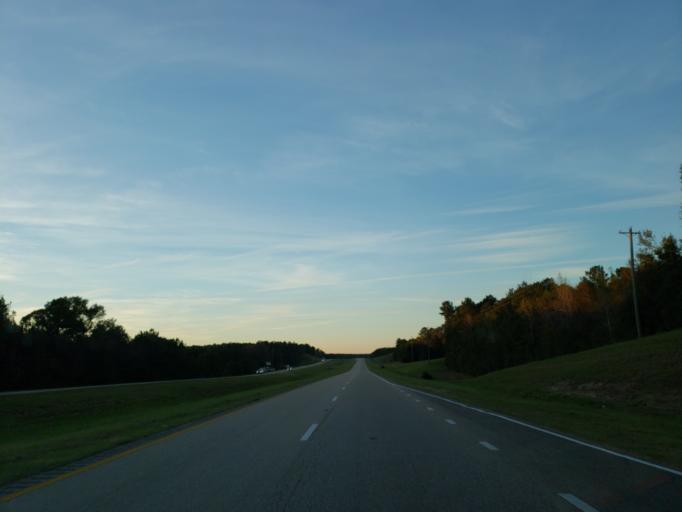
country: US
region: Mississippi
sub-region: Wayne County
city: Belmont
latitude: 31.4749
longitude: -88.4797
